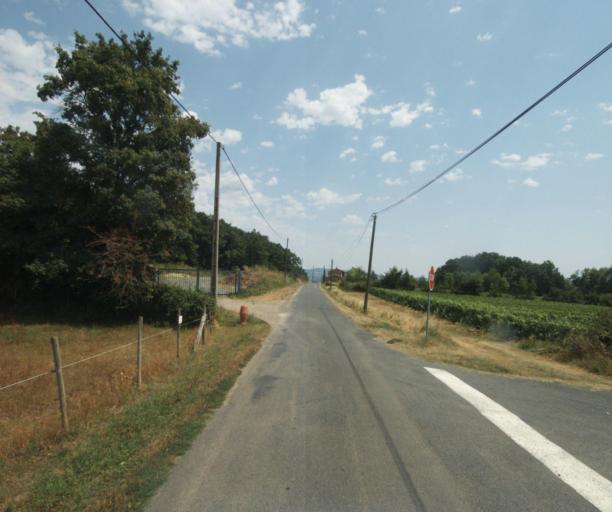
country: FR
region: Rhone-Alpes
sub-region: Departement du Rhone
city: Saint-Germain-Nuelles
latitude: 45.8674
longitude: 4.6080
